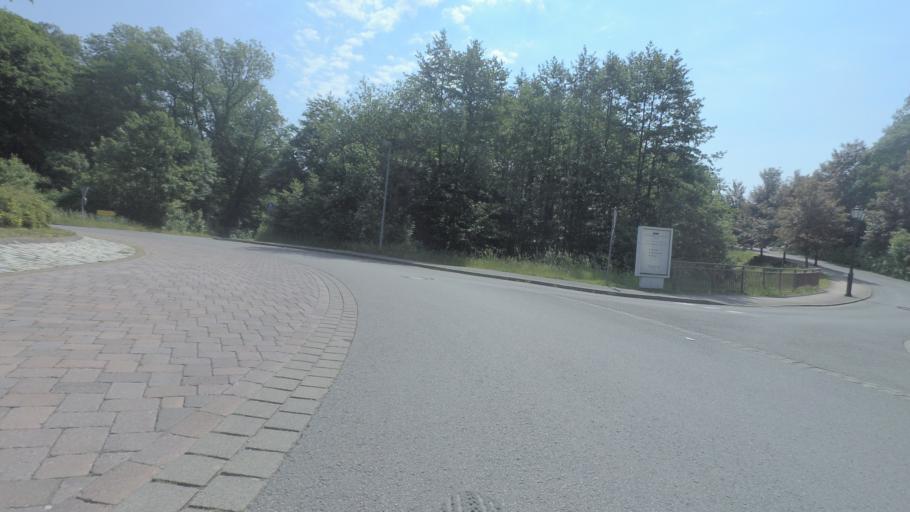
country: DE
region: Saxony-Anhalt
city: Huttenrode
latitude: 51.8064
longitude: 10.9181
